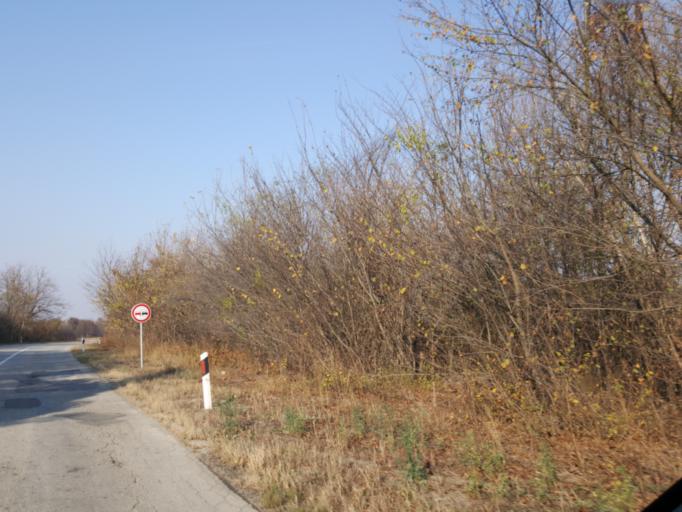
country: BG
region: Vidin
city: Bregovo
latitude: 44.1665
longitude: 22.5892
